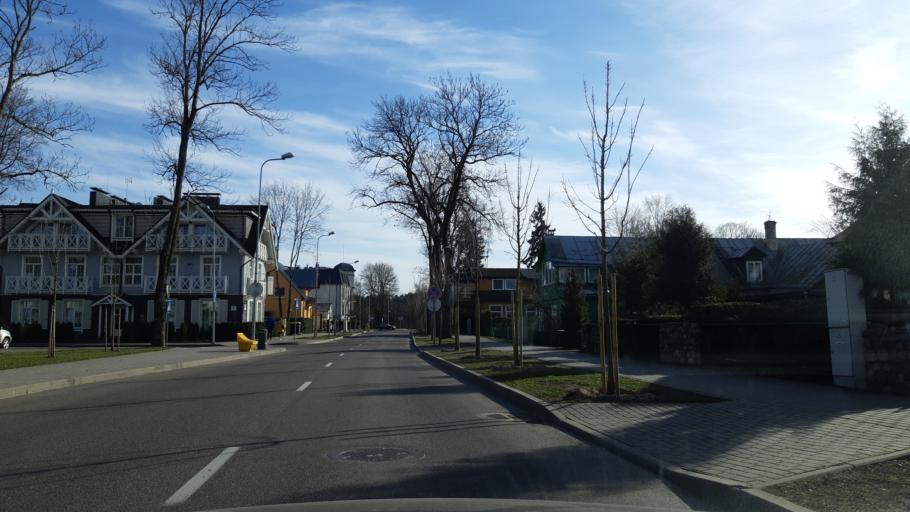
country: LT
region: Alytaus apskritis
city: Druskininkai
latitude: 54.0187
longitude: 23.9723
